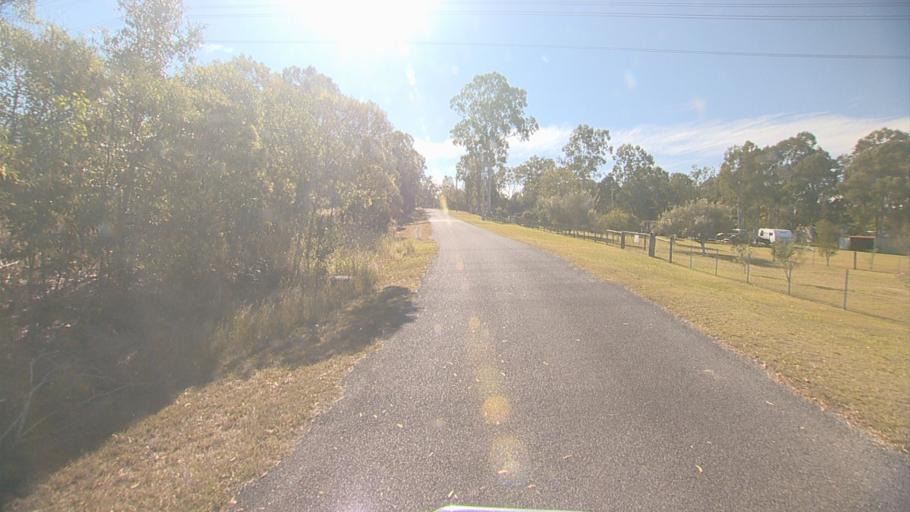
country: AU
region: Queensland
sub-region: Ipswich
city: Springfield Lakes
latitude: -27.7234
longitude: 152.9393
